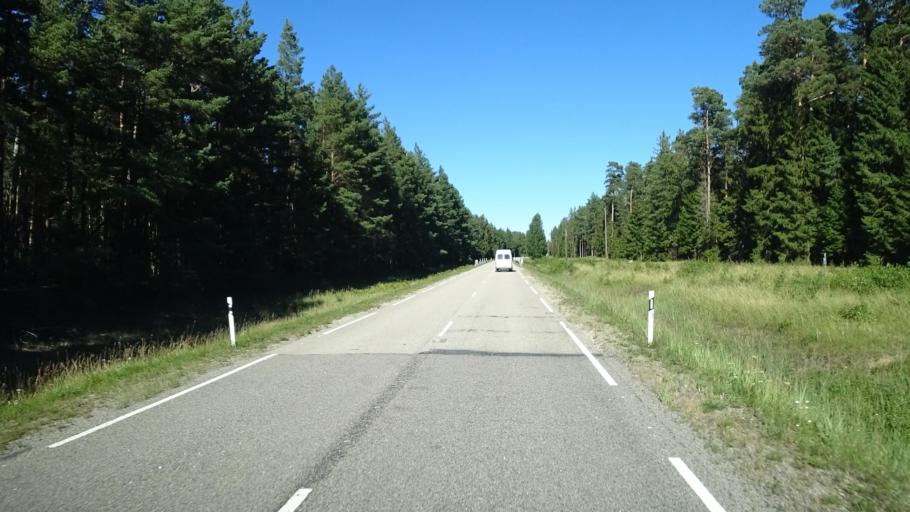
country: LV
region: Dundaga
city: Dundaga
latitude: 57.7224
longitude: 22.4832
